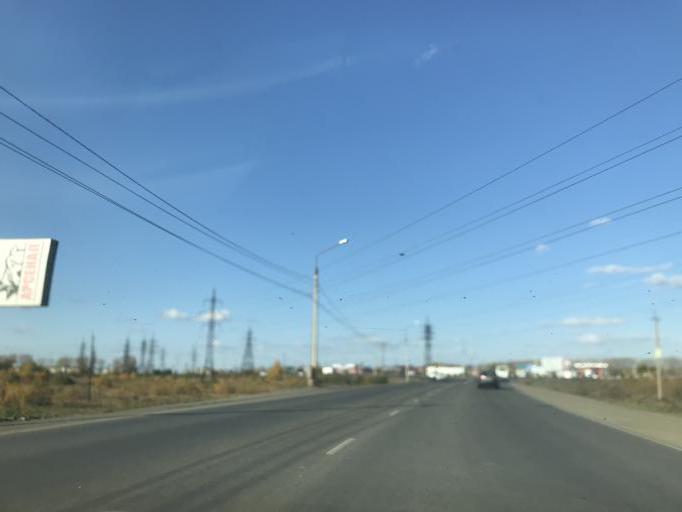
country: RU
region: Chelyabinsk
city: Roshchino
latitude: 55.2274
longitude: 61.2876
